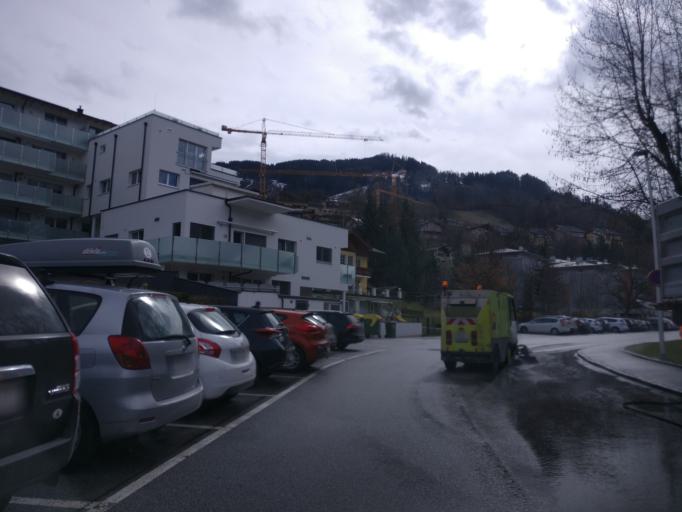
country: AT
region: Salzburg
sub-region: Politischer Bezirk Sankt Johann im Pongau
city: Sankt Johann im Pongau
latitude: 47.3469
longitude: 13.2041
